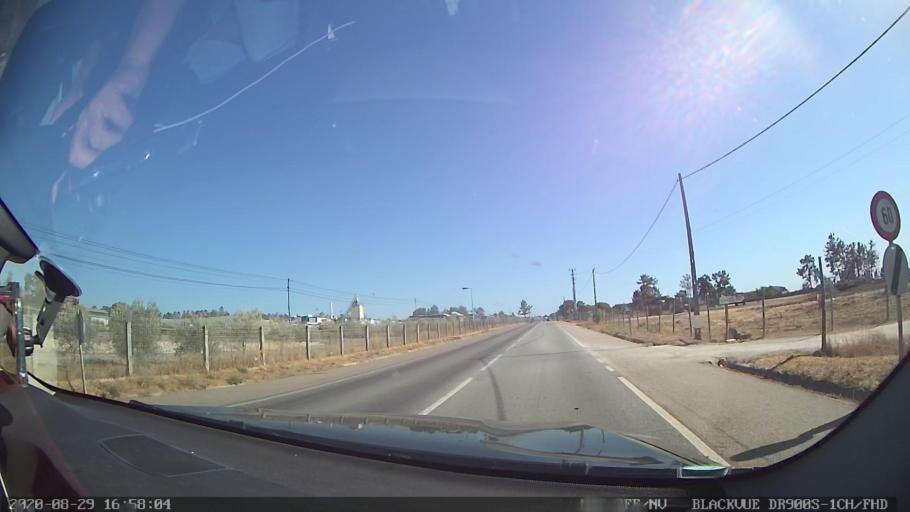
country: PT
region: Setubal
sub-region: Alcacer do Sal
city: Alcacer do Sal
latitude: 38.3990
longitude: -8.5147
